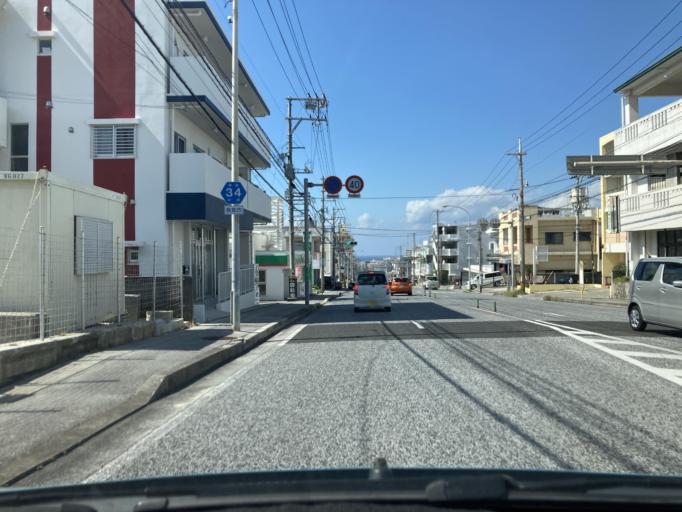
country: JP
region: Okinawa
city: Ginowan
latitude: 26.2564
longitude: 127.7528
